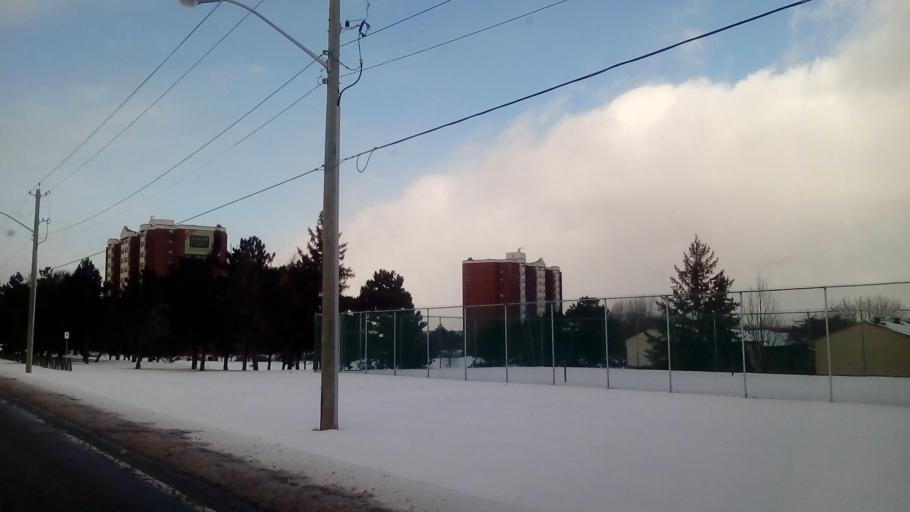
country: CA
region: Ontario
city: Ottawa
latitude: 45.3958
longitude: -75.6139
